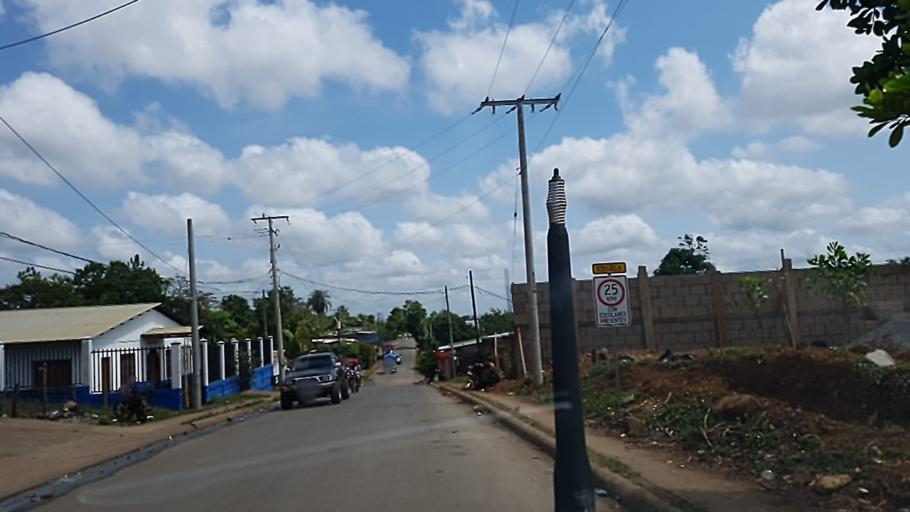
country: NI
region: Atlantico Sur
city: Nueva Guinea
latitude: 11.6865
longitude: -84.4607
